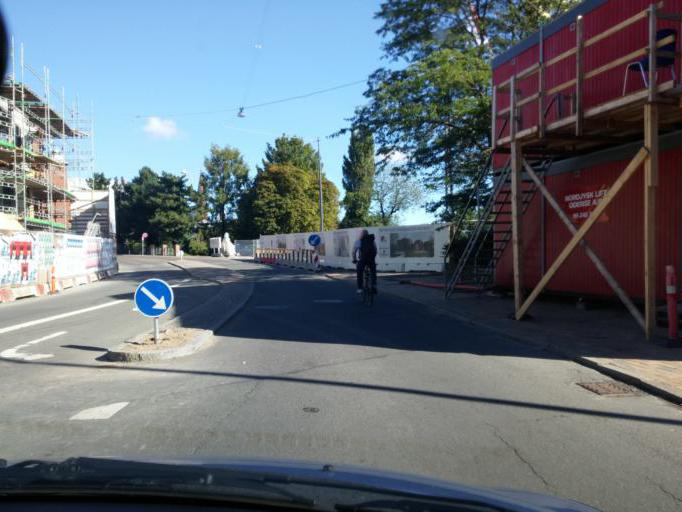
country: DK
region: South Denmark
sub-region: Odense Kommune
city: Odense
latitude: 55.3935
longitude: 10.3880
